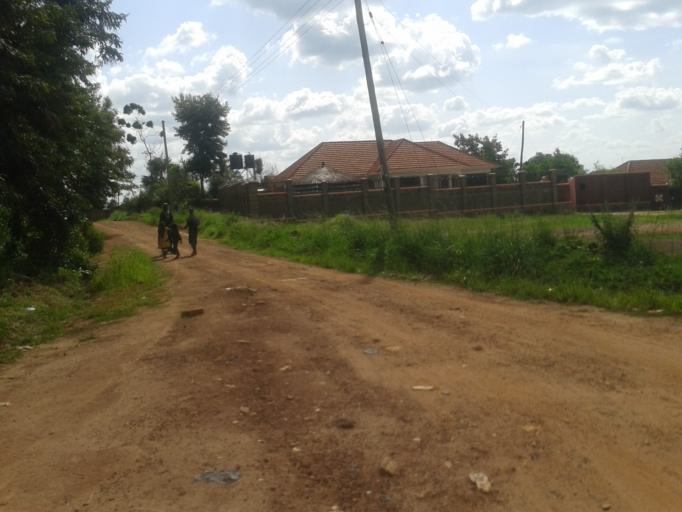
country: UG
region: Northern Region
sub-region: Gulu District
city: Gulu
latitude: 2.7829
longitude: 32.2974
